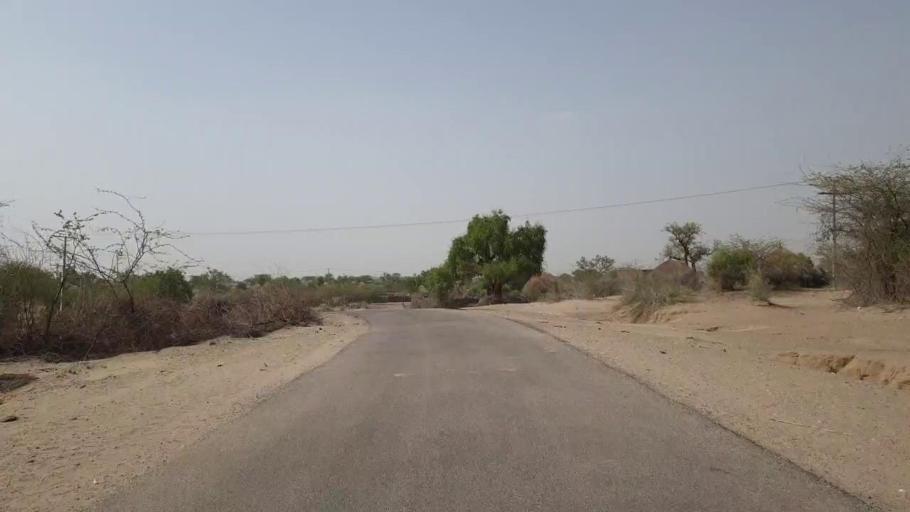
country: PK
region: Sindh
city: Mithi
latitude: 24.6105
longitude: 69.9207
